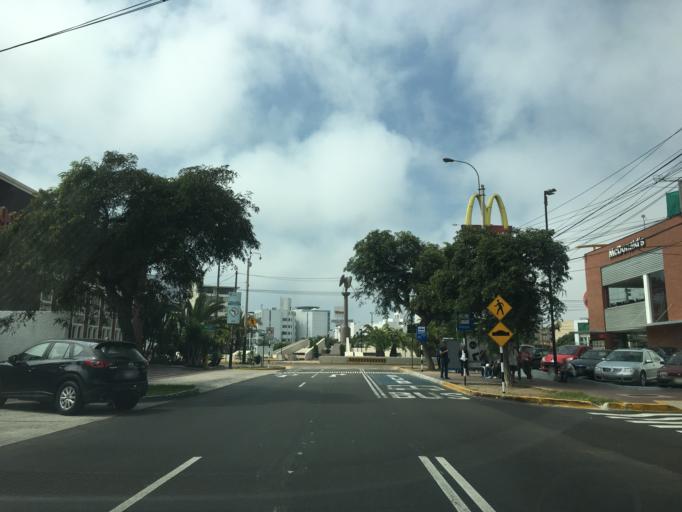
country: PE
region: Lima
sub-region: Lima
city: San Isidro
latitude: -12.1096
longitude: -77.0377
